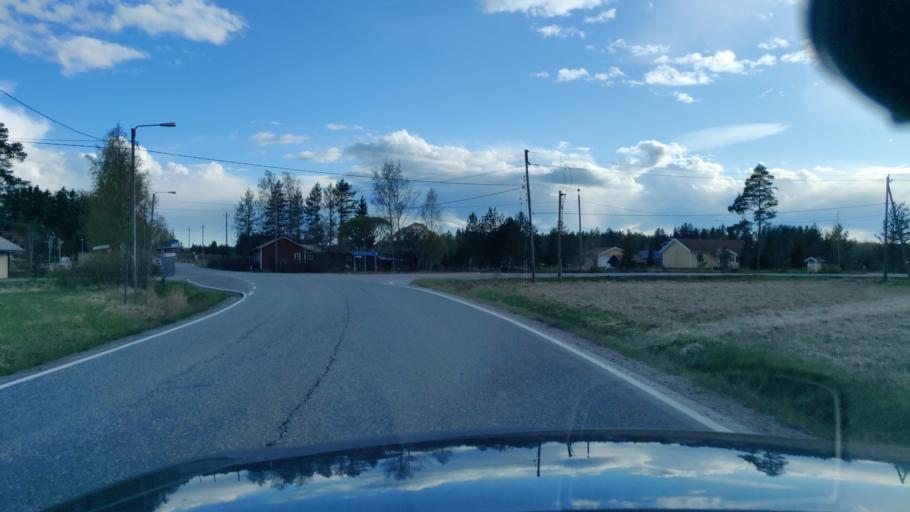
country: FI
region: Uusimaa
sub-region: Helsinki
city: Tuusula
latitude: 60.4541
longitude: 25.0223
